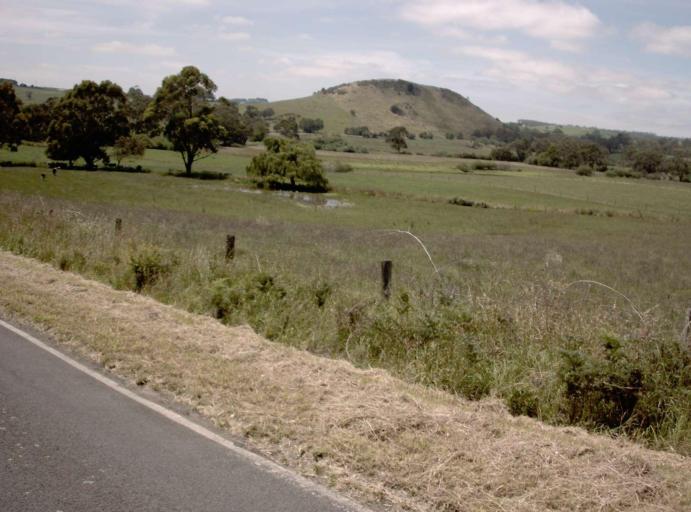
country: AU
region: Victoria
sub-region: Baw Baw
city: Warragul
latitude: -38.4817
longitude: 145.9834
